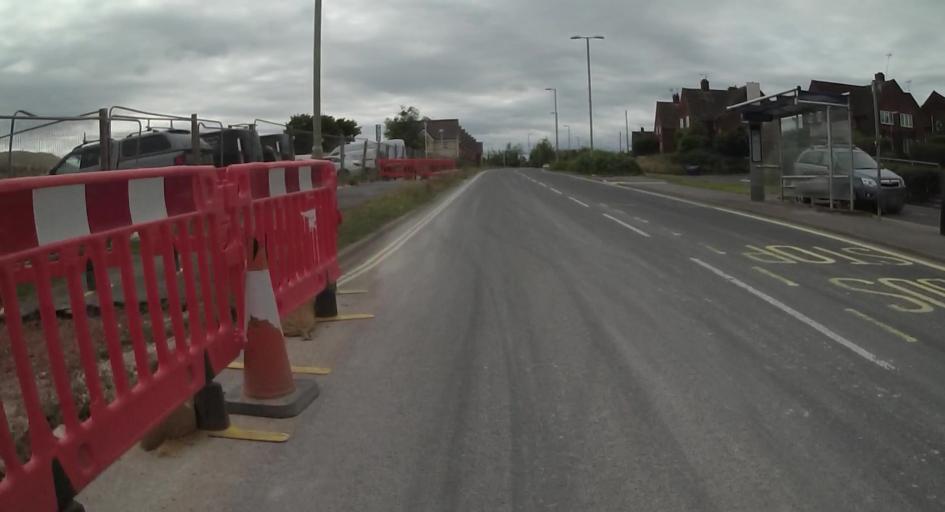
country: GB
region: England
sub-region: Hampshire
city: Basingstoke
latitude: 51.2708
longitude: -1.0961
